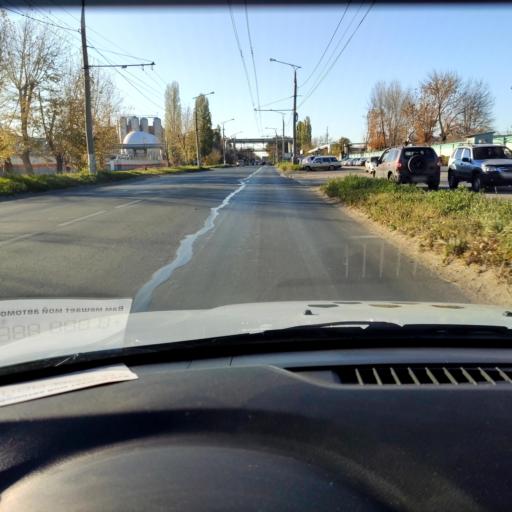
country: RU
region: Samara
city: Tol'yatti
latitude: 53.5467
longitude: 49.4466
